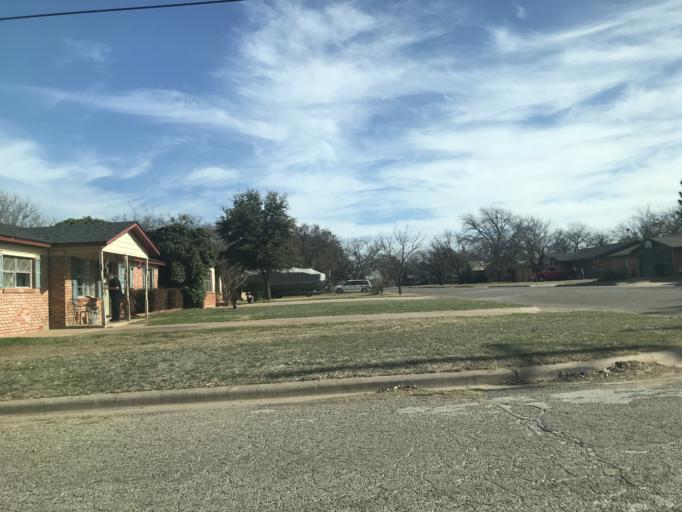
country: US
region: Texas
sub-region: Taylor County
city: Abilene
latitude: 32.4213
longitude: -99.7557
